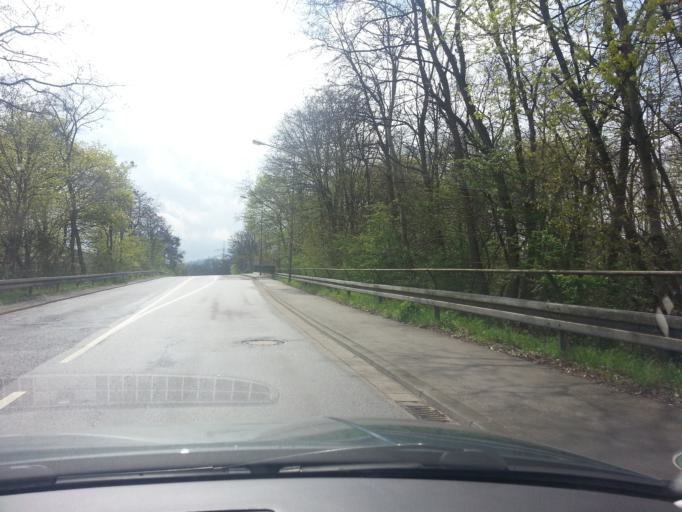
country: DE
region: Saarland
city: Homburg
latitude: 49.3118
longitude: 7.3196
